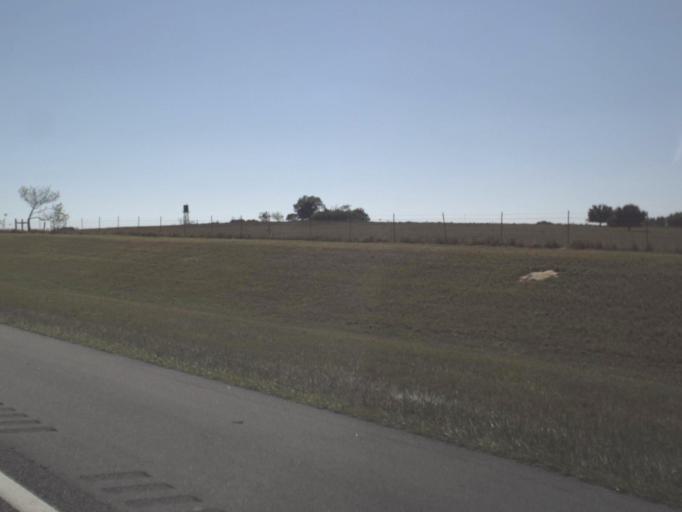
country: US
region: Florida
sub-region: Lake County
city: Hawthorne
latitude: 28.7134
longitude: -81.8947
